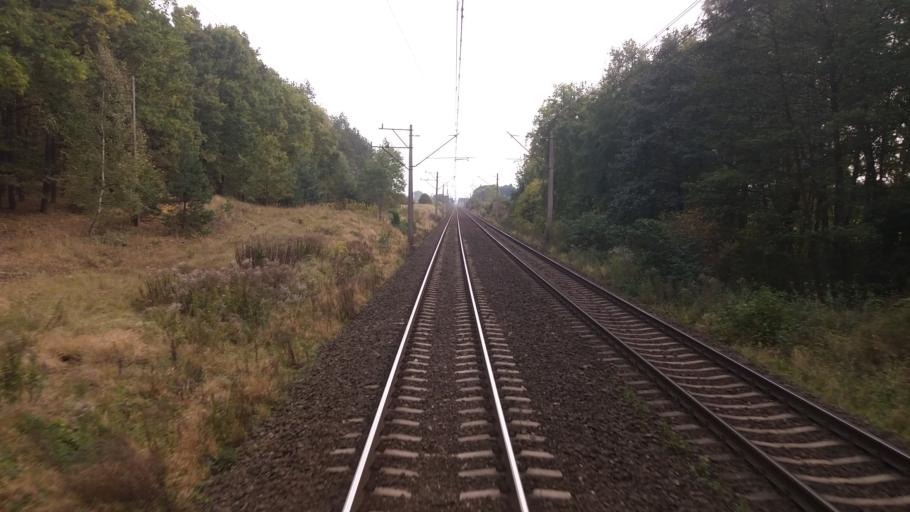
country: PL
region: West Pomeranian Voivodeship
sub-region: Powiat stargardzki
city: Dolice
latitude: 53.2056
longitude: 15.1848
